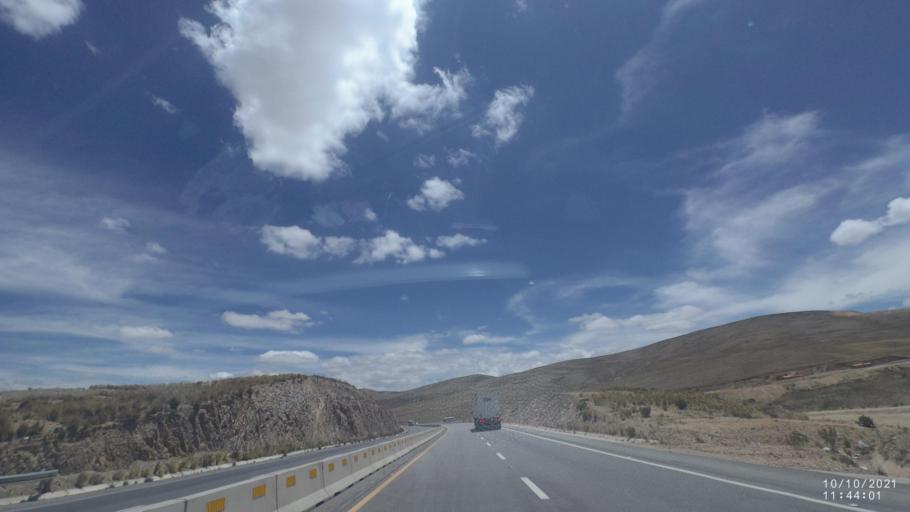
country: BO
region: Cochabamba
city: Colchani
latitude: -17.6696
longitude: -66.7587
